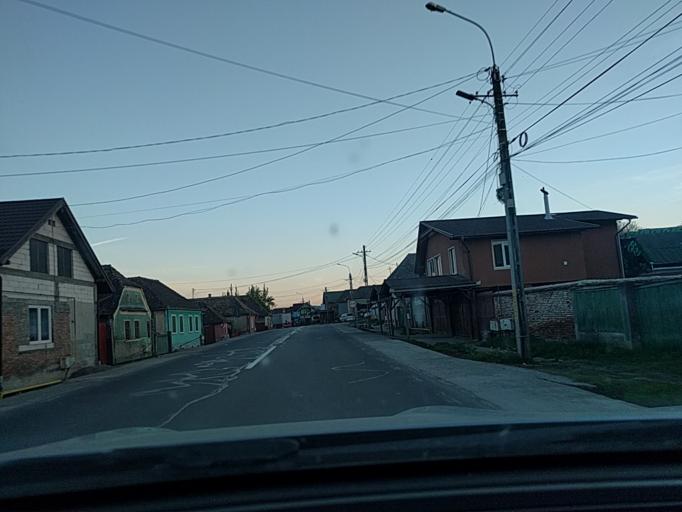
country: RO
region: Mures
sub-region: Comuna Balauseri
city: Chendu
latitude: 46.3841
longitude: 24.7290
